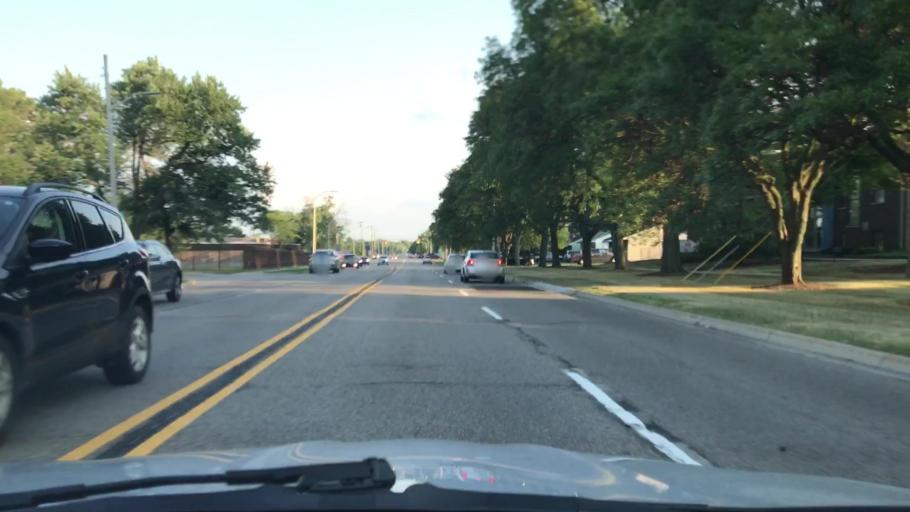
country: US
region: Michigan
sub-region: Oakland County
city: Clawson
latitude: 42.5278
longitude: -83.1653
